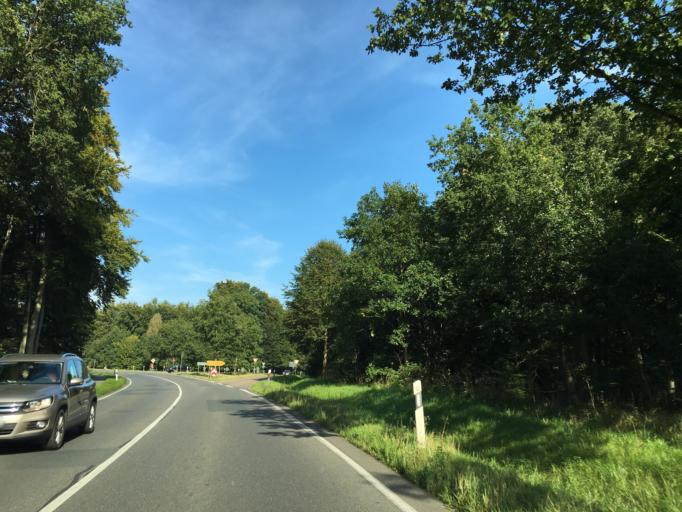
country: DE
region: Lower Saxony
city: Scharnebeck
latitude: 53.2809
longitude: 10.4905
